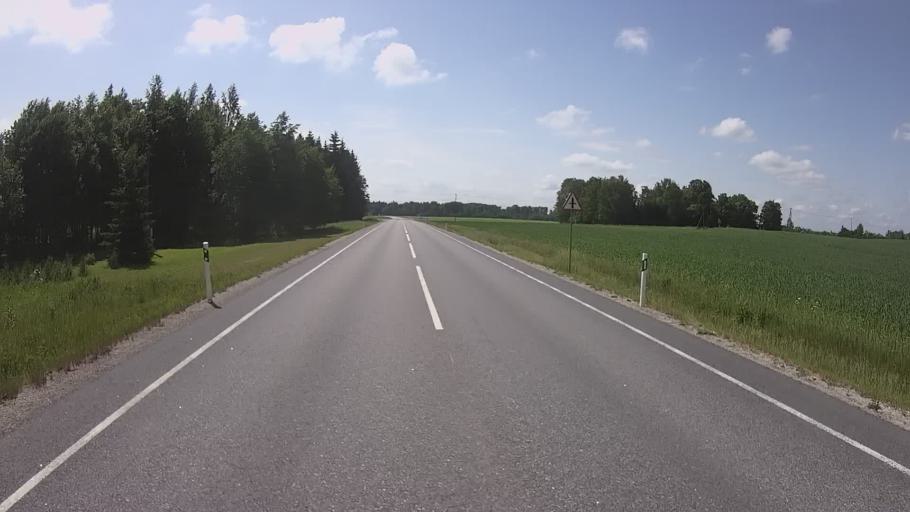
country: EE
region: Tartu
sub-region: Tartu linn
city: Tartu
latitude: 58.3808
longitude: 26.8863
